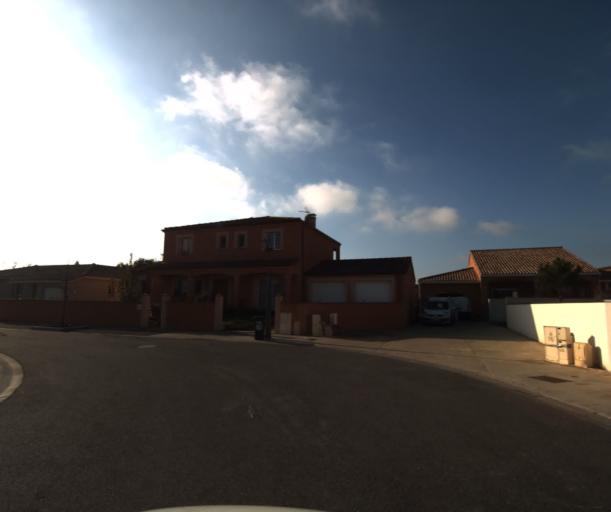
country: FR
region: Midi-Pyrenees
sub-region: Departement de la Haute-Garonne
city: Colomiers
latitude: 43.5923
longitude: 1.3535
